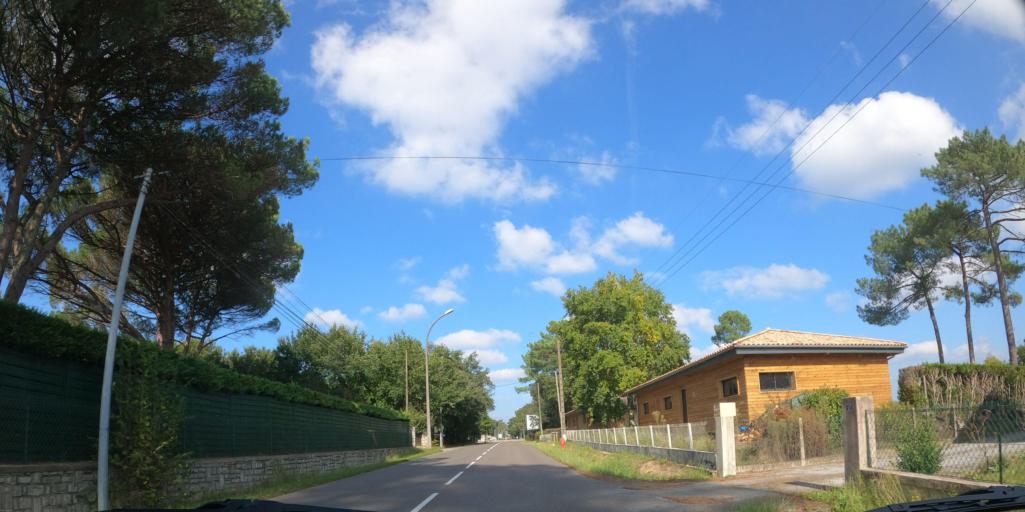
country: FR
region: Aquitaine
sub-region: Departement des Landes
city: Soustons
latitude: 43.7427
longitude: -1.3357
